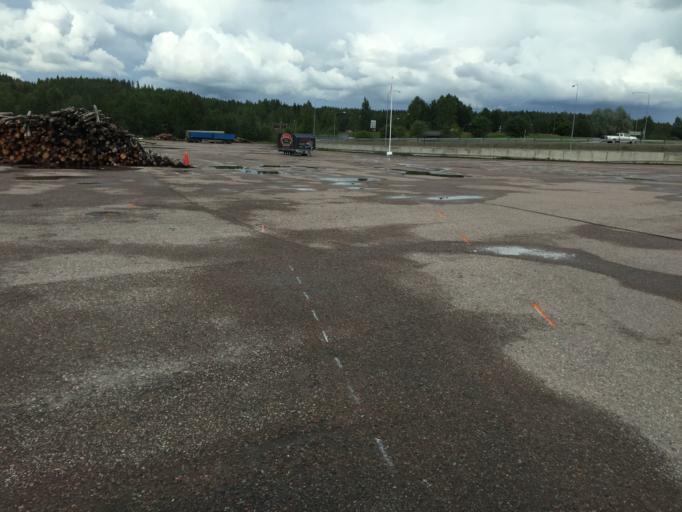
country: SE
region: Dalarna
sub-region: Vansbro Kommun
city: Vansbro
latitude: 60.5110
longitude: 14.2336
